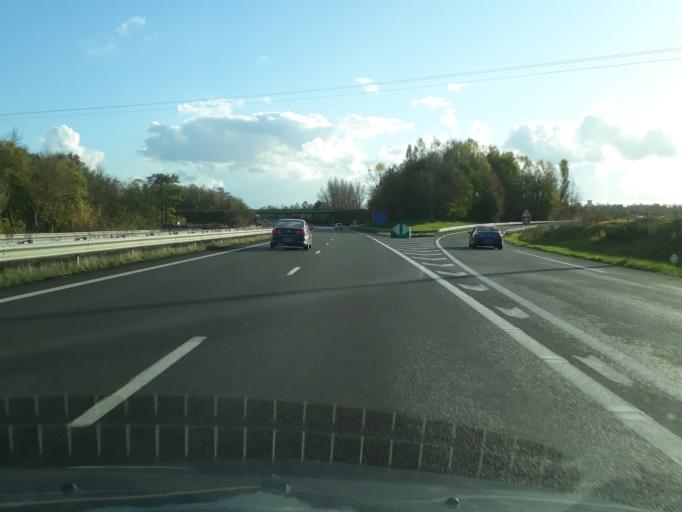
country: FR
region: Champagne-Ardenne
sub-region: Departement de la Marne
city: Fagnieres
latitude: 48.9733
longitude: 4.2843
